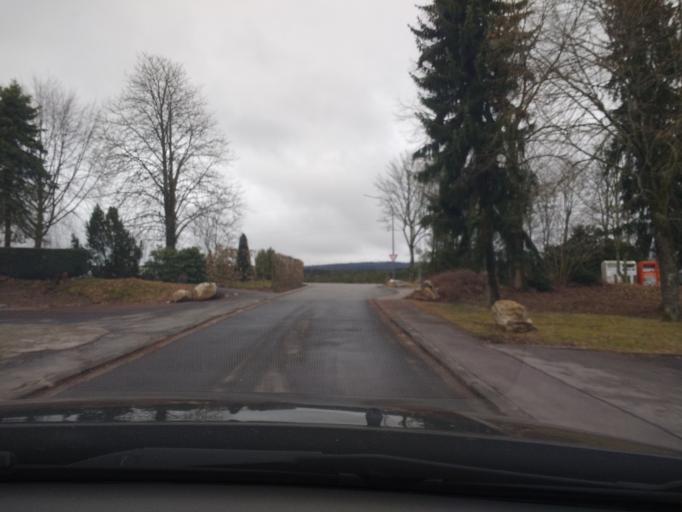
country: DE
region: Rheinland-Pfalz
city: Kell am See
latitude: 49.6304
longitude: 6.8241
